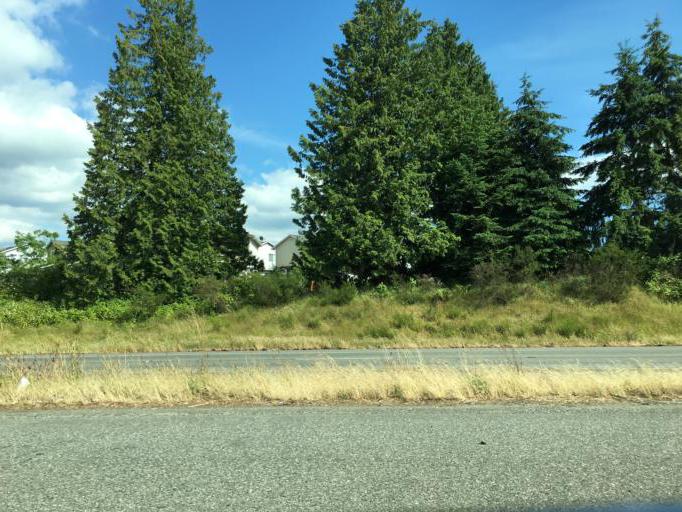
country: US
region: Washington
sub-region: Snohomish County
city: Alderwood Manor
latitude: 47.8277
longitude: -122.2660
